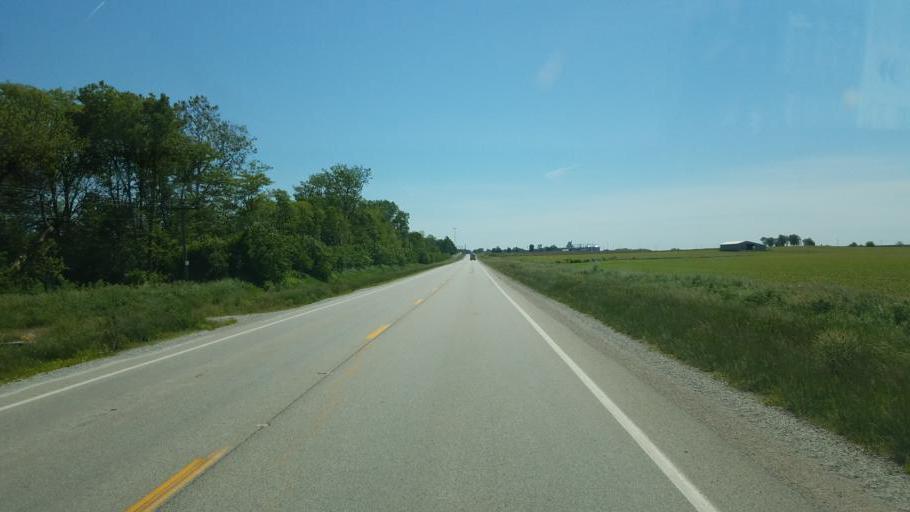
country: US
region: Illinois
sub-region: McLean County
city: Heyworth
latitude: 40.3121
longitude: -89.0117
